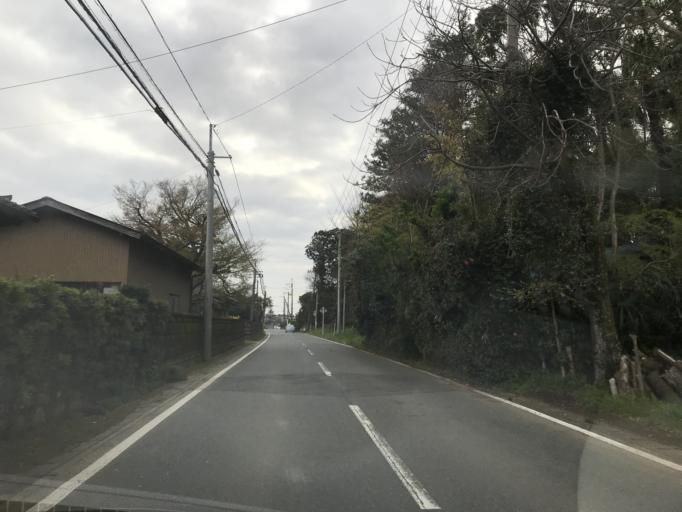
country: JP
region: Chiba
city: Omigawa
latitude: 35.8021
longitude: 140.5674
